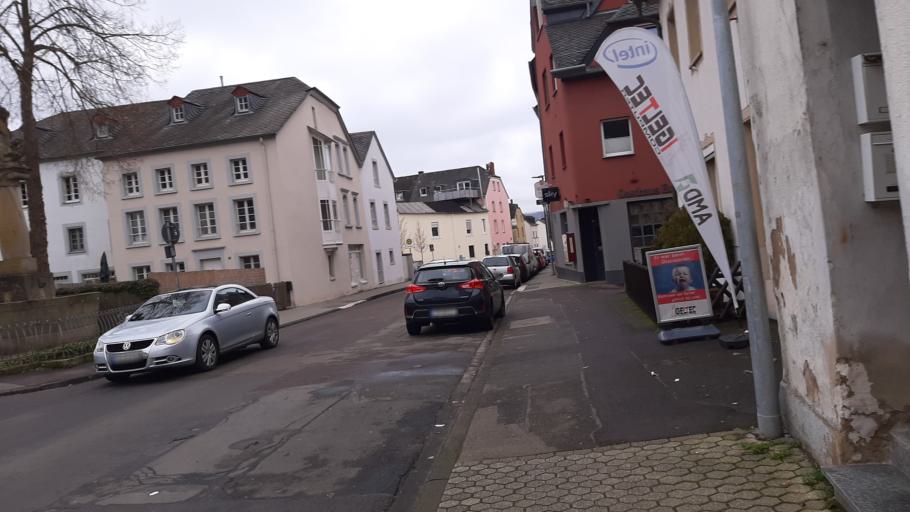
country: DE
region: Rheinland-Pfalz
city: Trier
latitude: 49.7409
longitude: 6.6077
